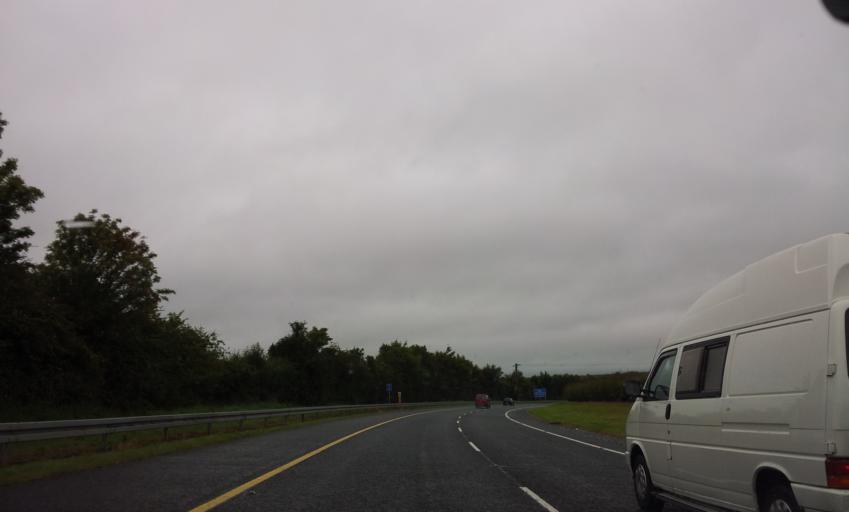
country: IE
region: Munster
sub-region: County Cork
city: Passage West
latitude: 51.9214
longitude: -8.3840
